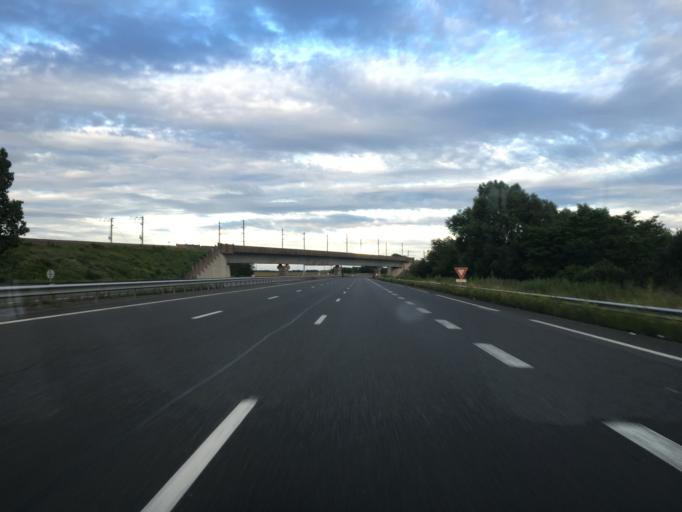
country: FR
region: Ile-de-France
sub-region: Departement de Seine-et-Marne
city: Moisenay
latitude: 48.5848
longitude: 2.7278
